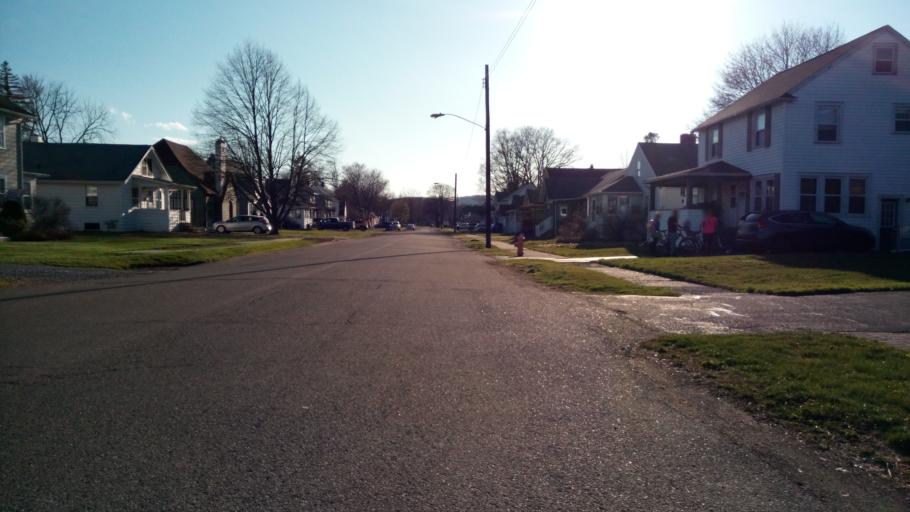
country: US
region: New York
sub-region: Chemung County
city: Elmira
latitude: 42.0759
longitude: -76.7857
